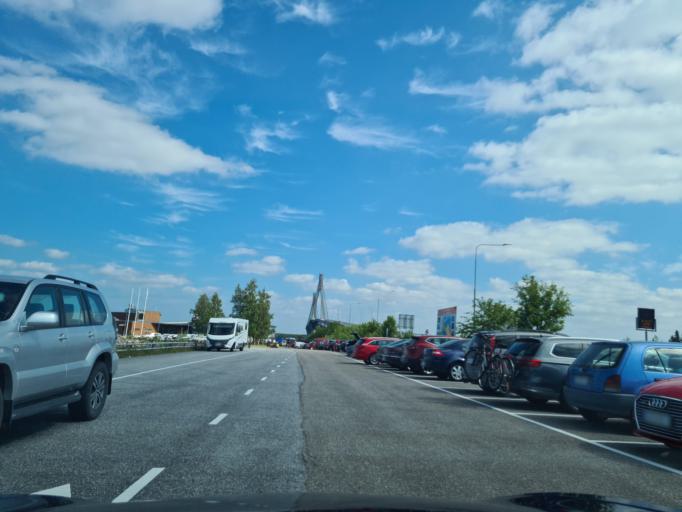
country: FI
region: Ostrobothnia
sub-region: Vaasa
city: Replot
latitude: 63.2069
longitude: 21.4587
